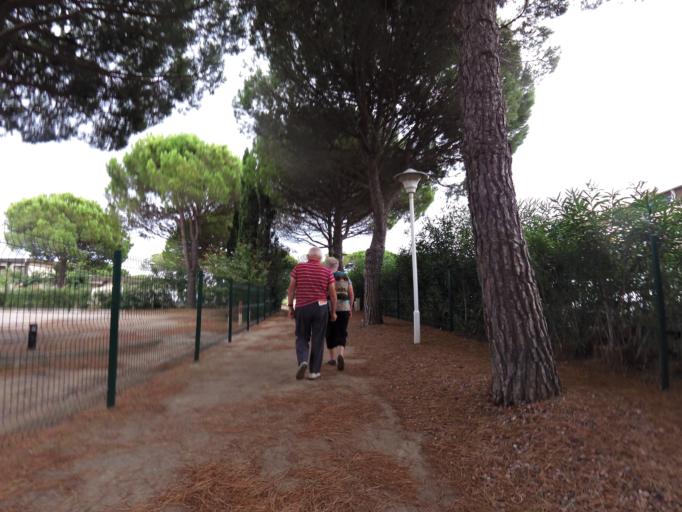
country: FR
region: Languedoc-Roussillon
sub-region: Departement du Gard
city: Le Grau-du-Roi
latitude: 43.5236
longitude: 4.1385
